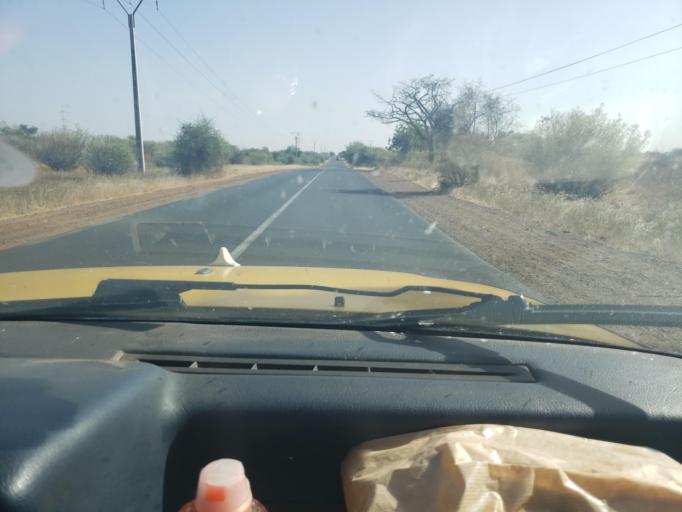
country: SN
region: Louga
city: Louga
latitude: 15.6615
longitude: -16.2580
